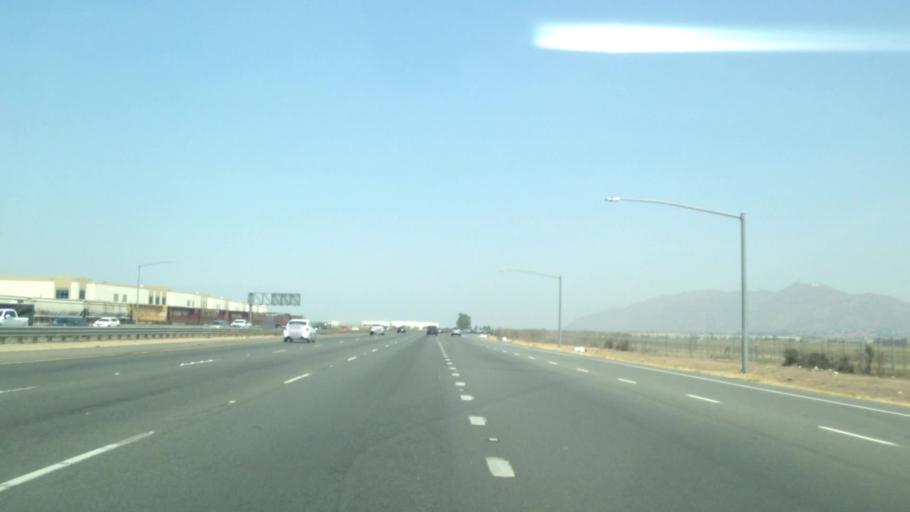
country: US
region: California
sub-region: Riverside County
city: March Air Force Base
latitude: 33.8905
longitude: -117.2712
